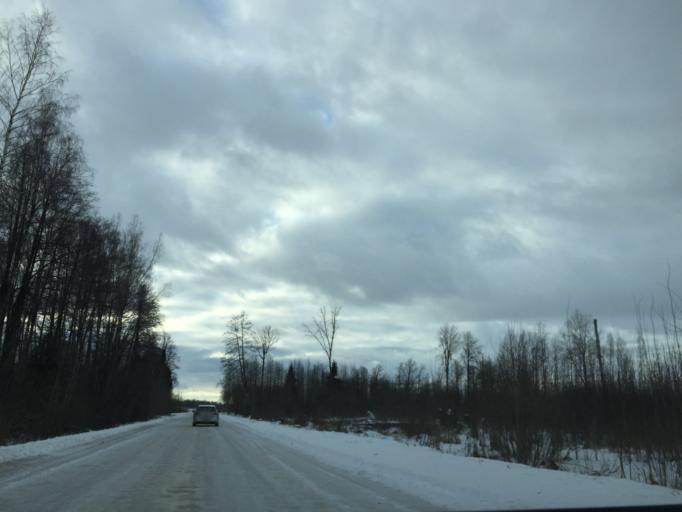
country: LV
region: Lielvarde
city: Lielvarde
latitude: 56.5923
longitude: 24.7373
